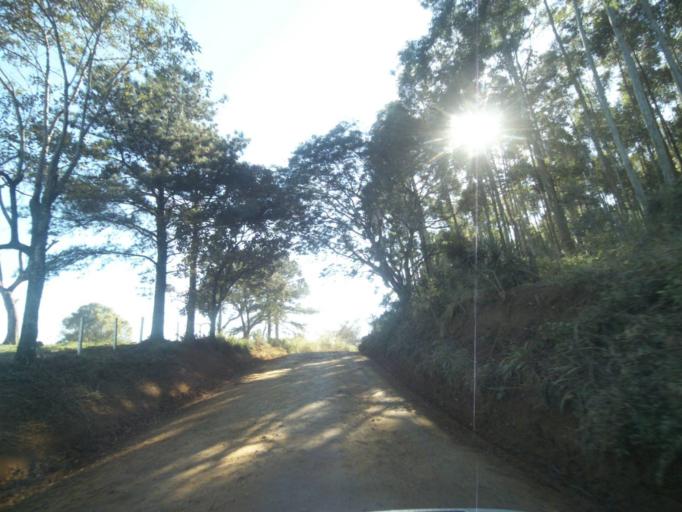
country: BR
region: Parana
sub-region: Tibagi
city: Tibagi
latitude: -24.5370
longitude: -50.4756
